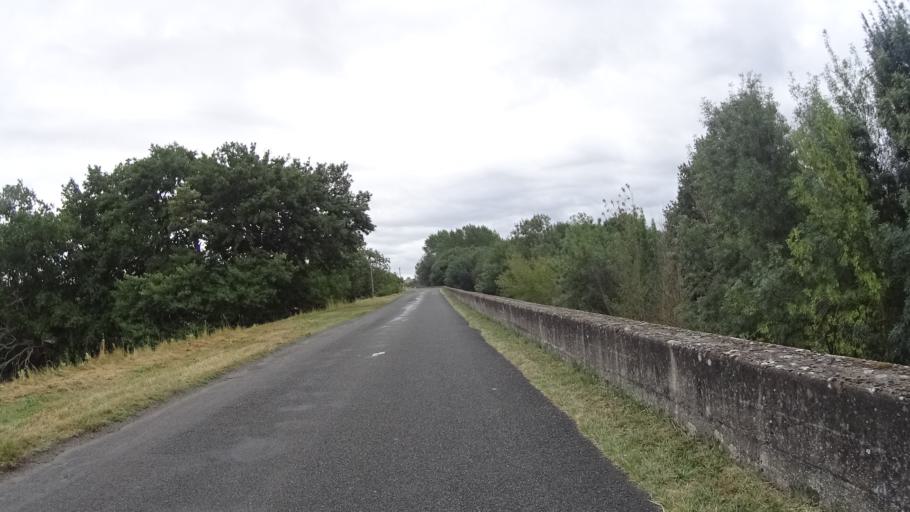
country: FR
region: Pays de la Loire
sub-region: Departement de Maine-et-Loire
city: Chalonnes-sur-Loire
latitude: 47.3663
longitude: -0.7338
